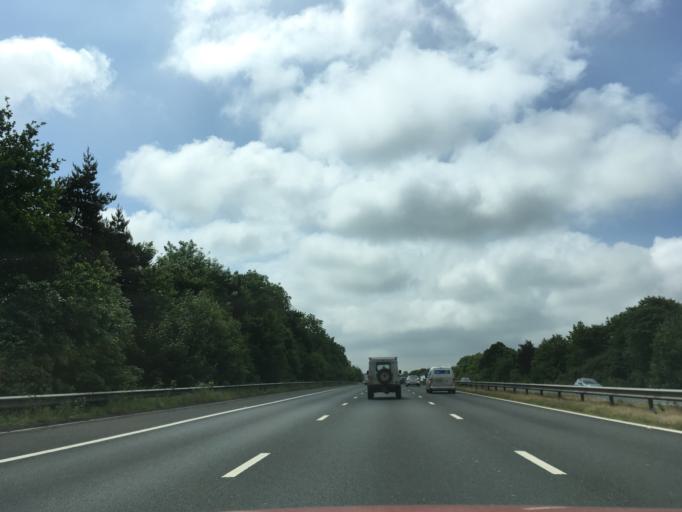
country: GB
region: England
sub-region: Devon
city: Cullompton
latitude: 50.8962
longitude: -3.3739
